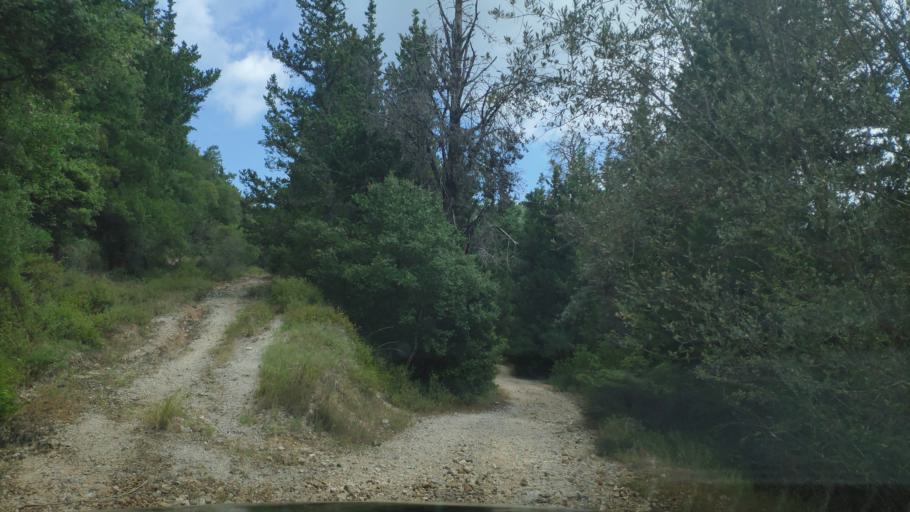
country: GR
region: Ionian Islands
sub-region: Lefkada
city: Lefkada
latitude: 38.8008
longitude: 20.6723
